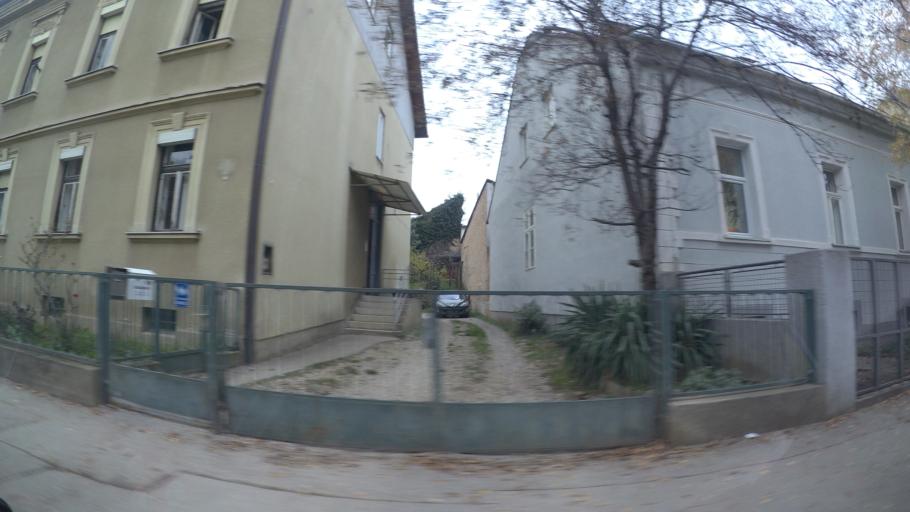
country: HR
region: Grad Zagreb
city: Zagreb - Centar
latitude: 45.8134
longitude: 15.9523
